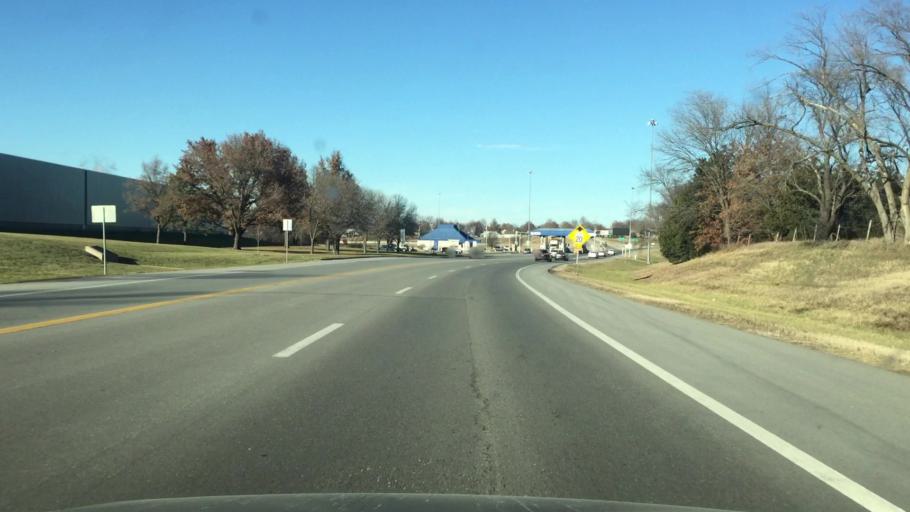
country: US
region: Kansas
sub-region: Douglas County
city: Lawrence
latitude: 38.9848
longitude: -95.2581
